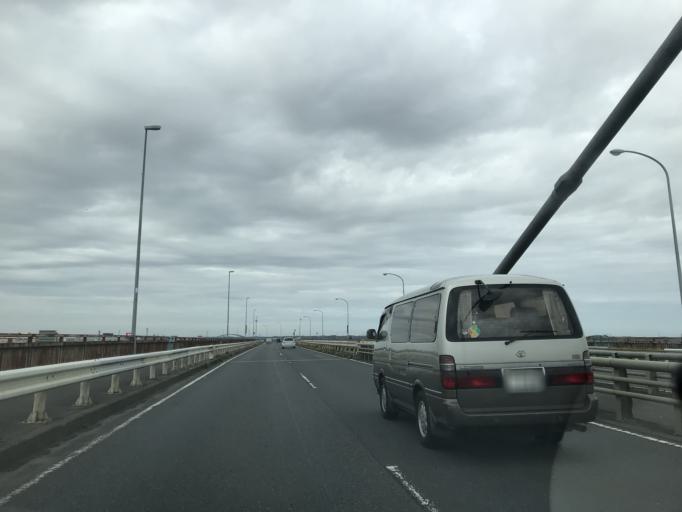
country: JP
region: Chiba
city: Katori-shi
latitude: 35.9083
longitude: 140.4908
